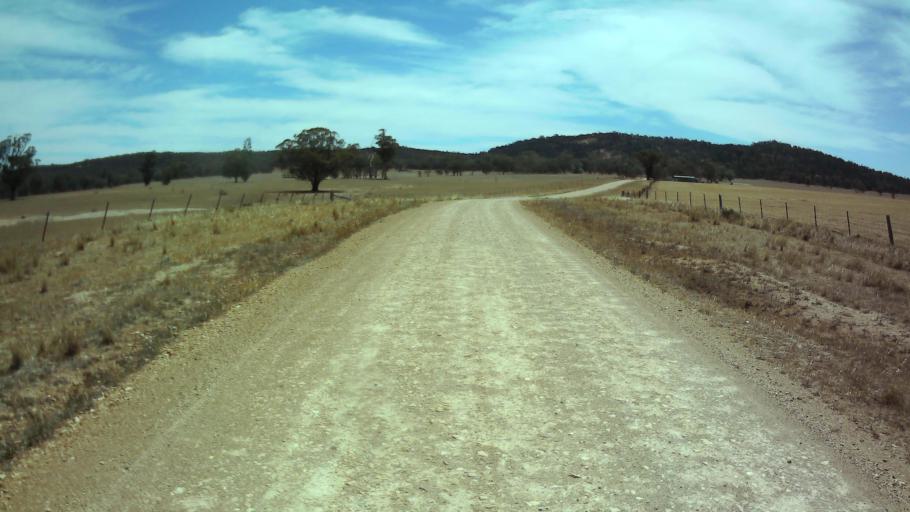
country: AU
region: New South Wales
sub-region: Weddin
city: Grenfell
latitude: -33.7493
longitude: 148.2056
